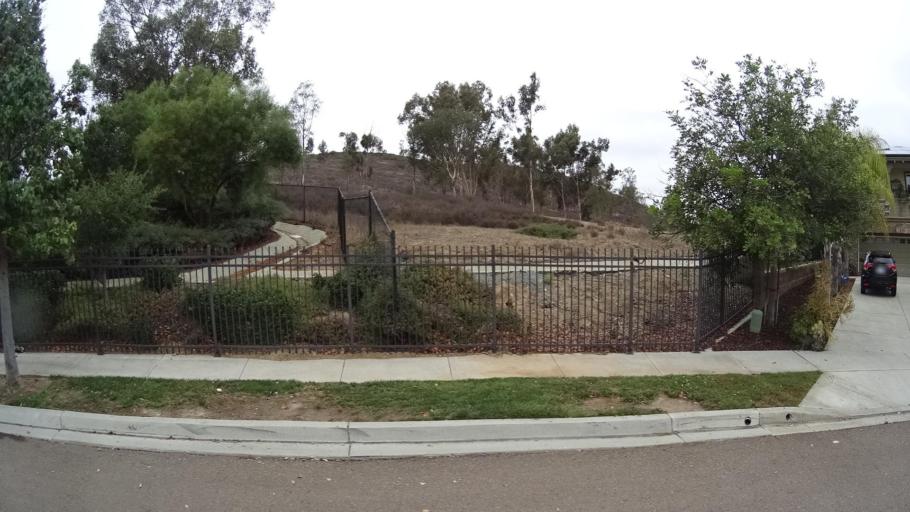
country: US
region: California
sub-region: San Diego County
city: Fairbanks Ranch
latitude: 33.0301
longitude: -117.1138
